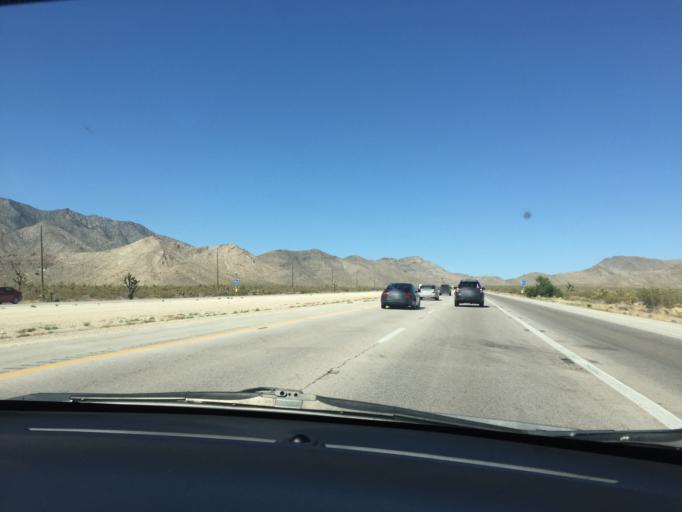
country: US
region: Nevada
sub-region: Clark County
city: Sandy Valley
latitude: 35.4620
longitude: -115.6227
